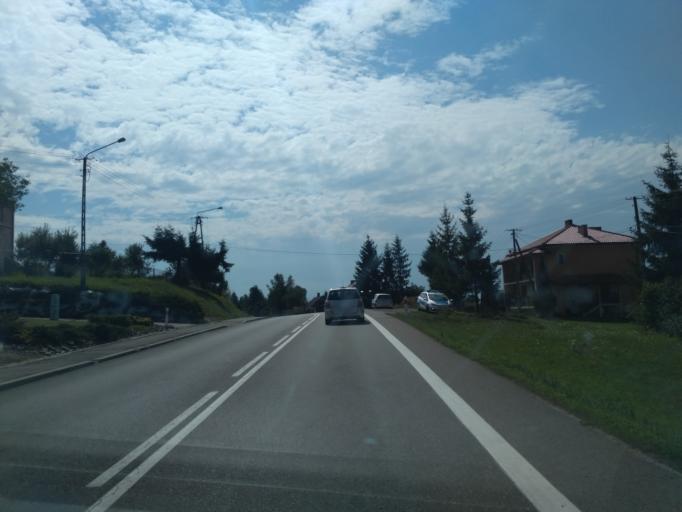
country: PL
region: Subcarpathian Voivodeship
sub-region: Powiat brzozowski
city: Blizne
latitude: 49.7547
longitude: 21.9706
